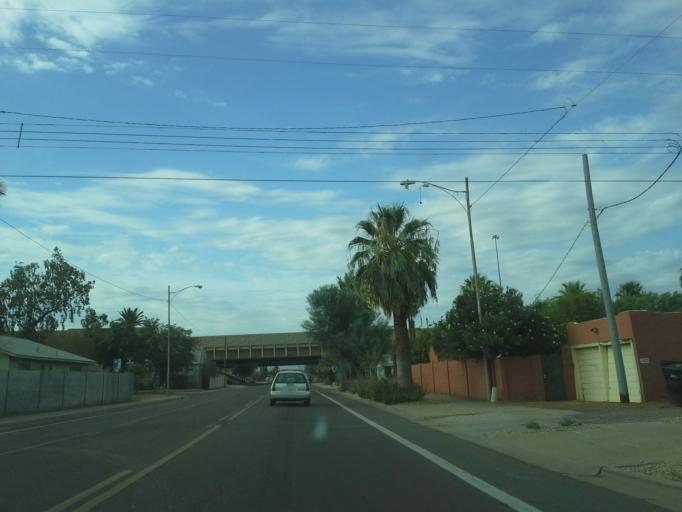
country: US
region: Arizona
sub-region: Maricopa County
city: Phoenix
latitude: 33.4635
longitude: -112.0913
